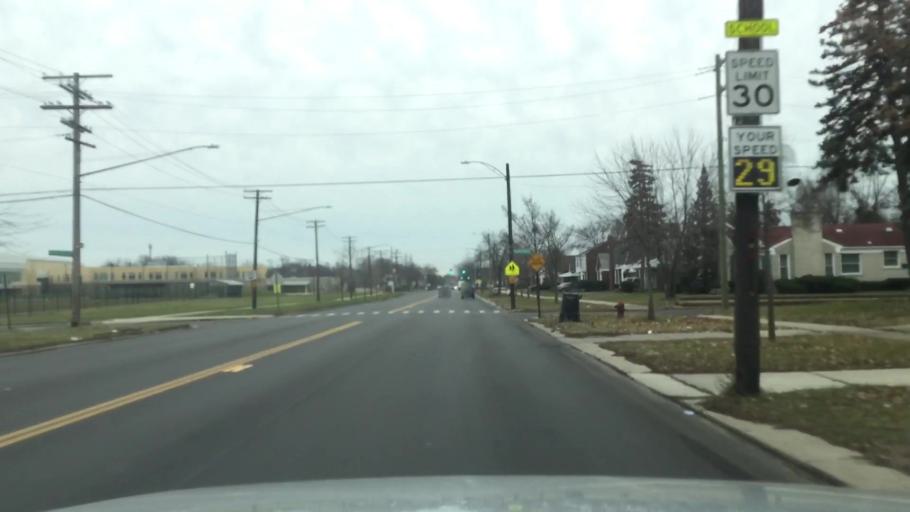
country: US
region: Michigan
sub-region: Wayne County
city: Harper Woods
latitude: 42.4098
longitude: -82.9323
